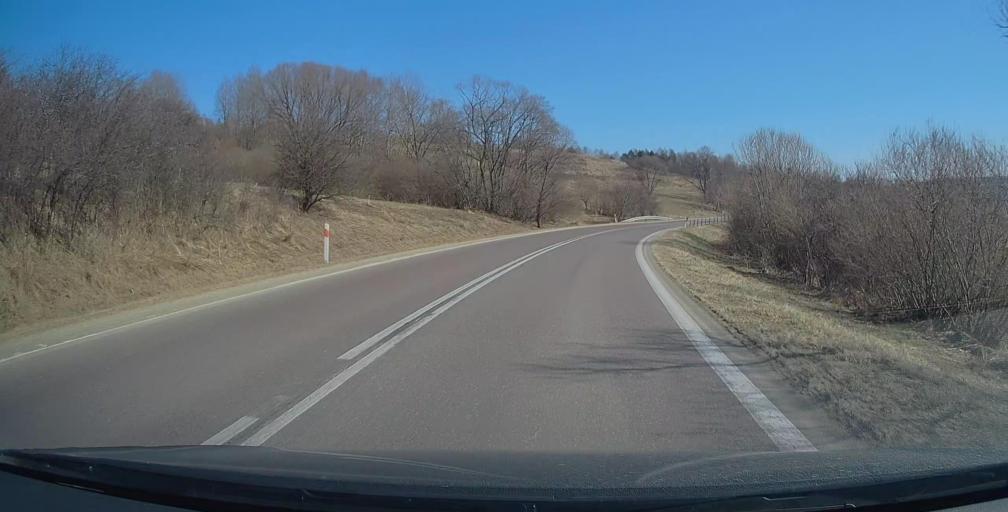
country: PL
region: Subcarpathian Voivodeship
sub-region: Powiat przemyski
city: Bircza
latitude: 49.5988
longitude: 22.4884
